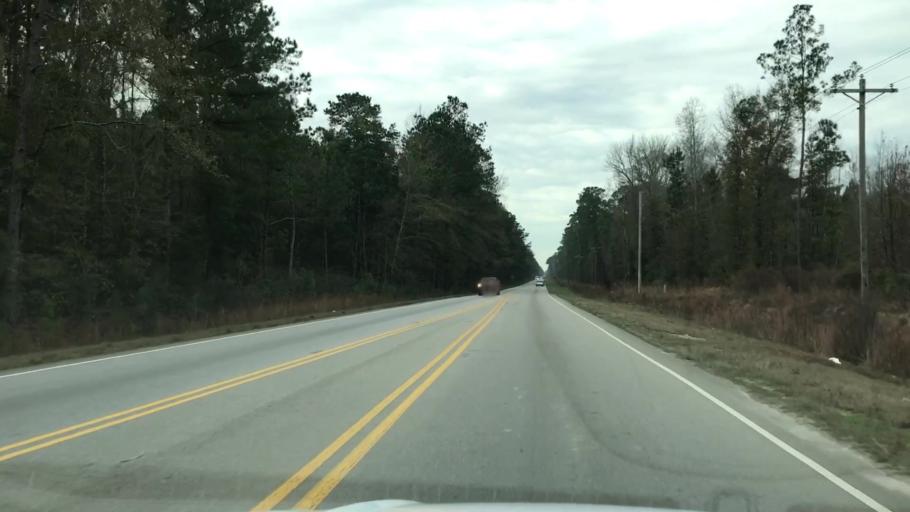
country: US
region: South Carolina
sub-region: Jasper County
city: Ridgeland
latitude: 32.3847
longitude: -80.9090
